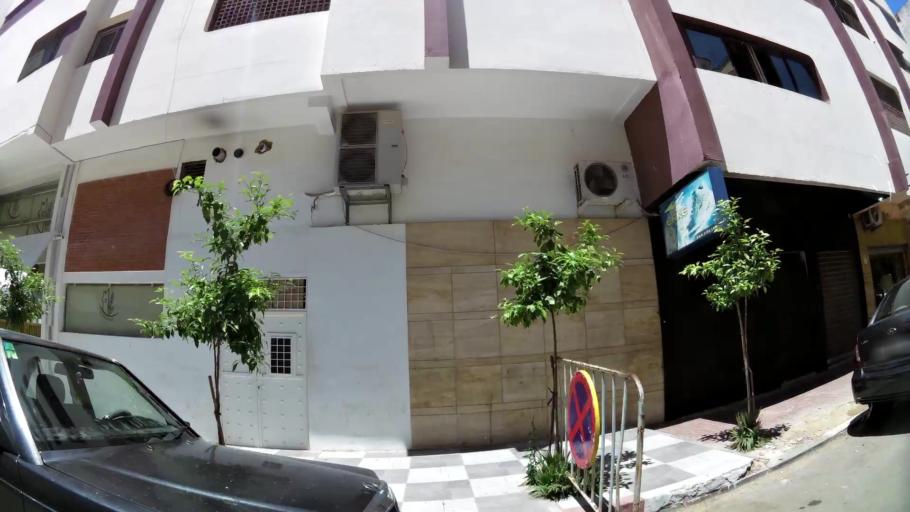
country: MA
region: Meknes-Tafilalet
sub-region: Meknes
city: Meknes
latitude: 33.8994
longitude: -5.5521
